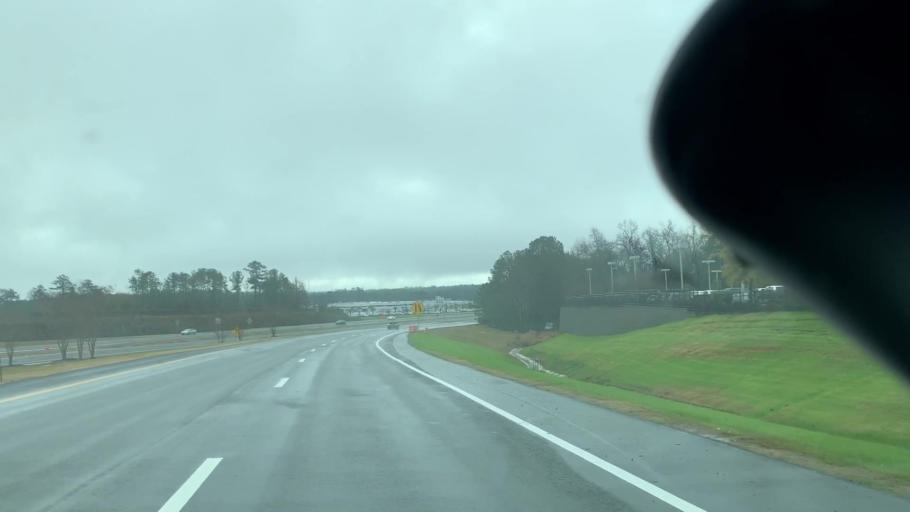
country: US
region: South Carolina
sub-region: Richland County
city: Dentsville
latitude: 34.1341
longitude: -80.9645
